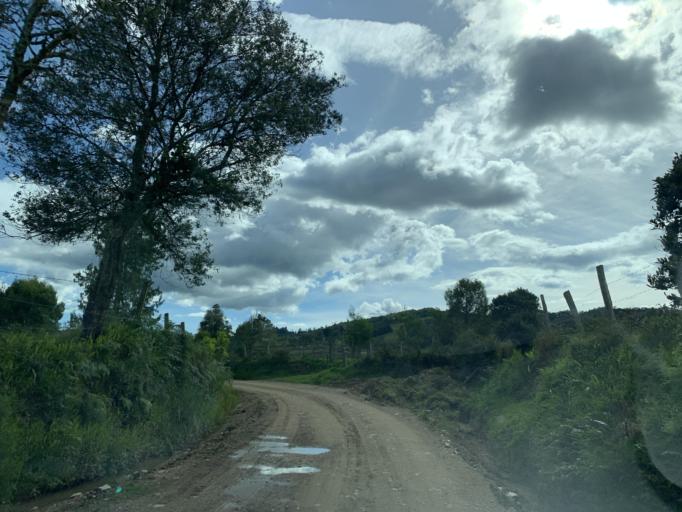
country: CO
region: Boyaca
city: Arcabuco
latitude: 5.7867
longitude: -73.4592
